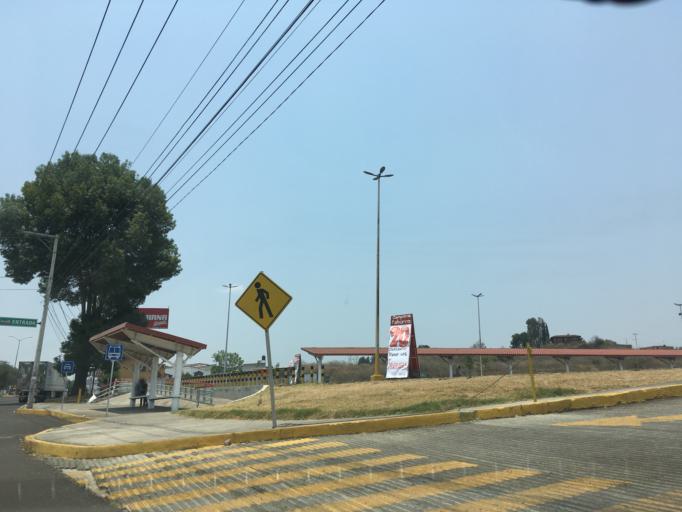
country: MX
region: Michoacan
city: Patzcuaro
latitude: 19.5201
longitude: -101.6168
